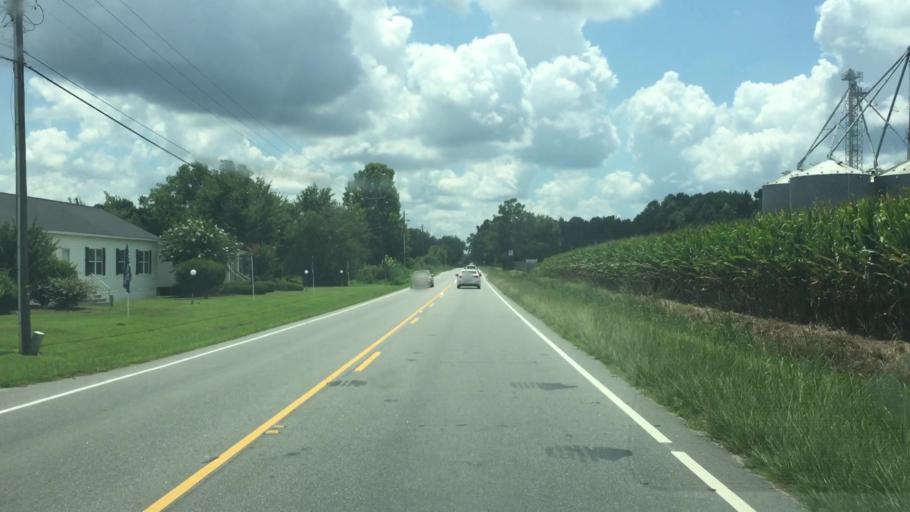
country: US
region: North Carolina
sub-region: Columbus County
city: Chadbourn
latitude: 34.3160
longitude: -78.8264
